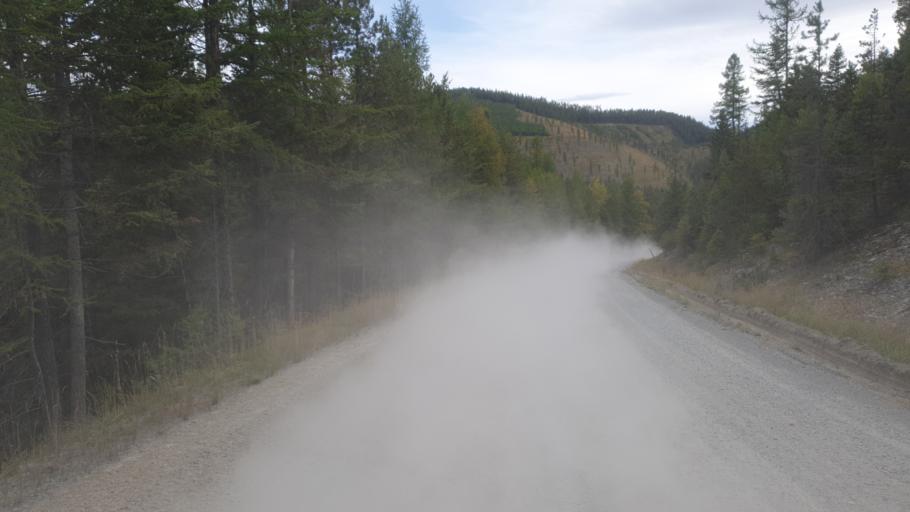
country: US
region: Montana
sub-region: Flathead County
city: Lakeside
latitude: 47.9932
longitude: -114.3197
